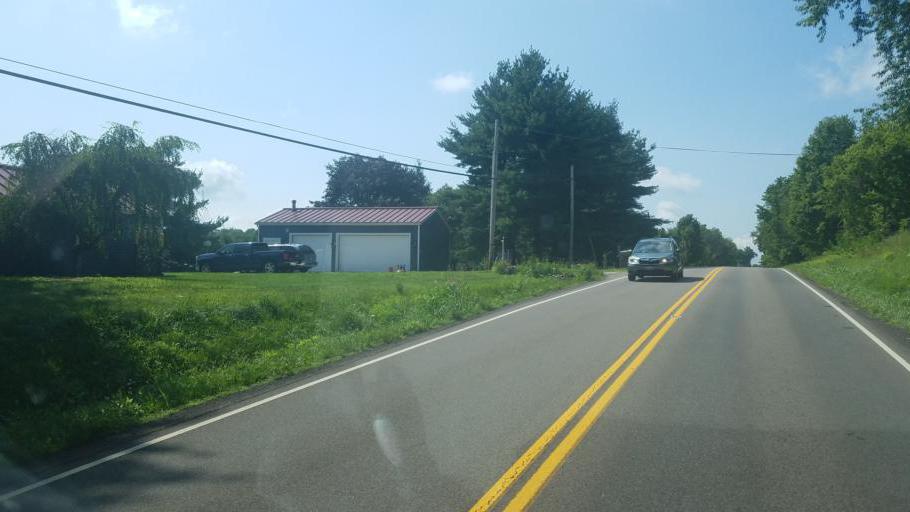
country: US
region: Ohio
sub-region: Licking County
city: Granville
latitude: 40.1166
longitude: -82.5183
